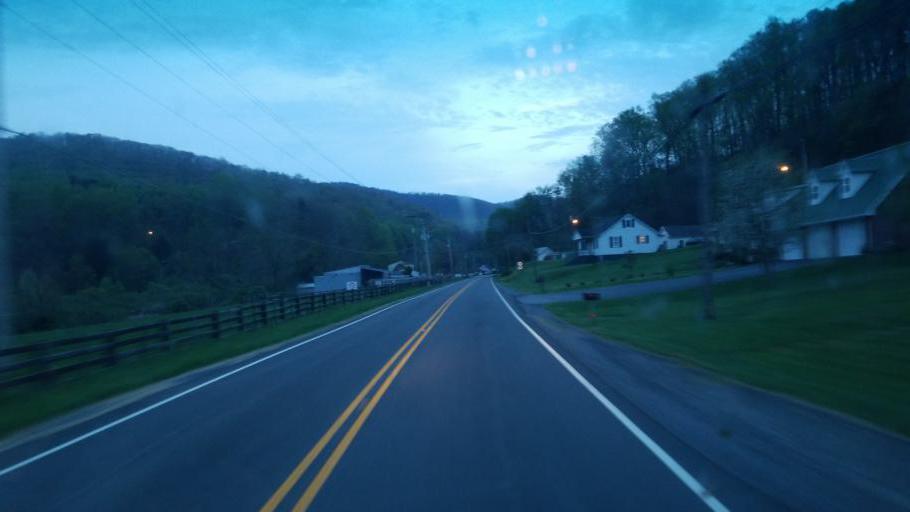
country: US
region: Virginia
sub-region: Smyth County
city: Marion
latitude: 36.8199
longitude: -81.4710
